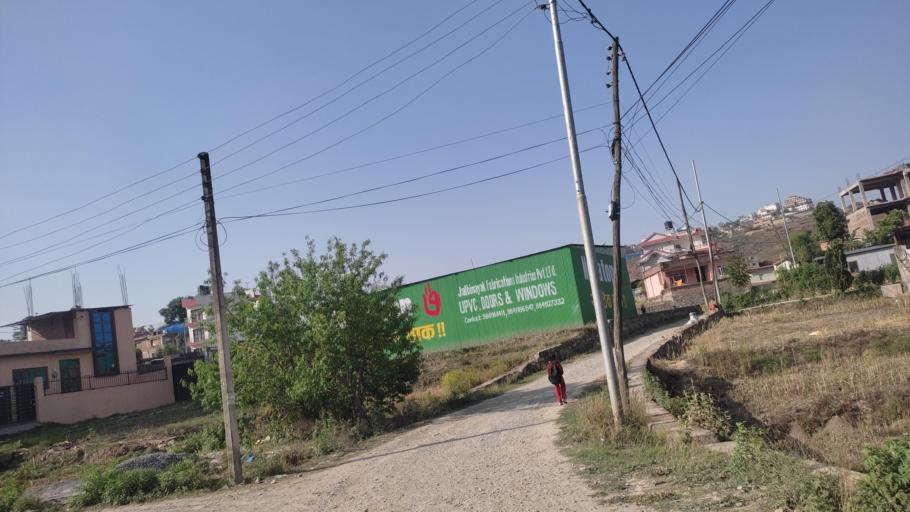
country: NP
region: Central Region
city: Kirtipur
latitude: 27.6554
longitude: 85.2856
